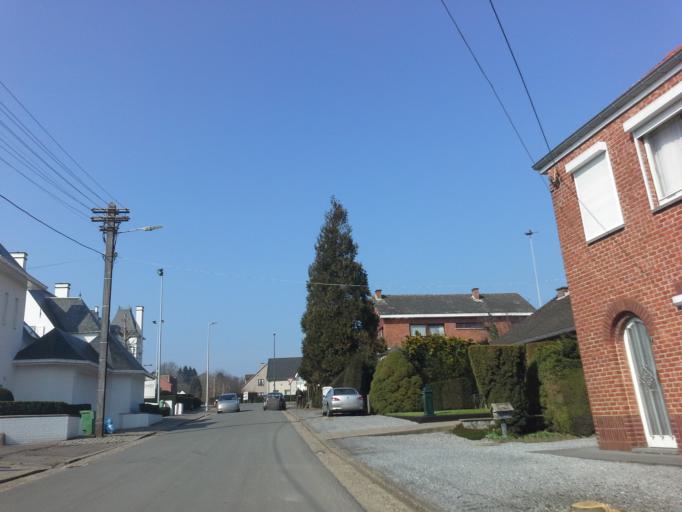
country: BE
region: Flanders
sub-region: Provincie Limburg
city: Hoeselt
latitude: 50.8464
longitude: 5.4893
